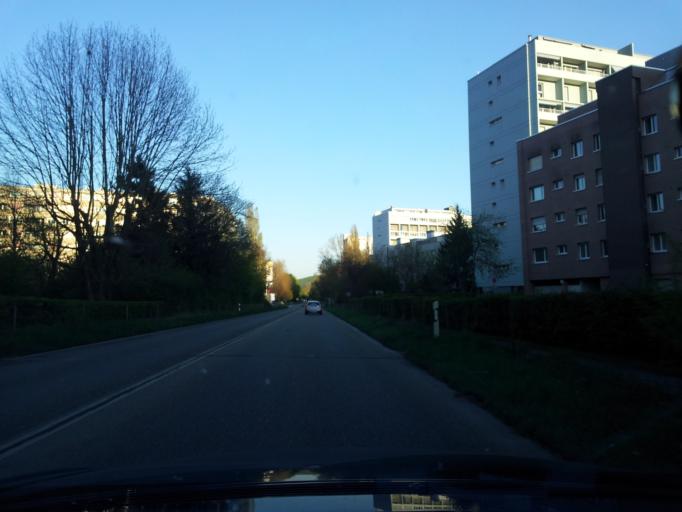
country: CH
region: Bern
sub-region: Biel/Bienne District
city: Nidau
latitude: 47.1261
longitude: 7.2480
